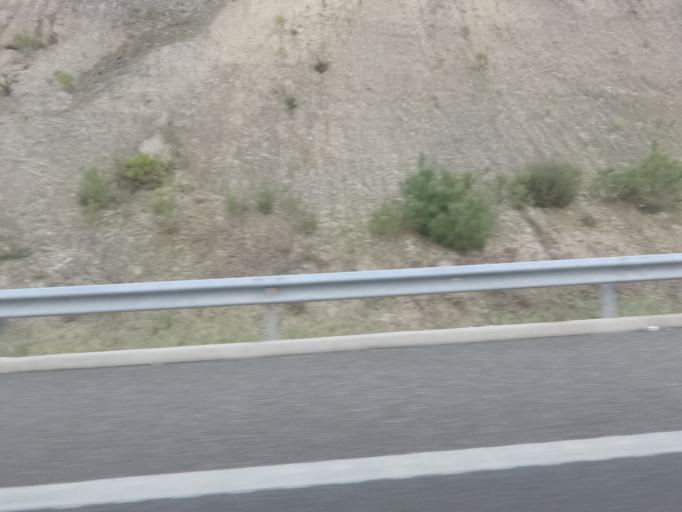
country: ES
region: Galicia
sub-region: Provincia de Ourense
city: Maside
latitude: 42.4528
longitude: -8.0244
